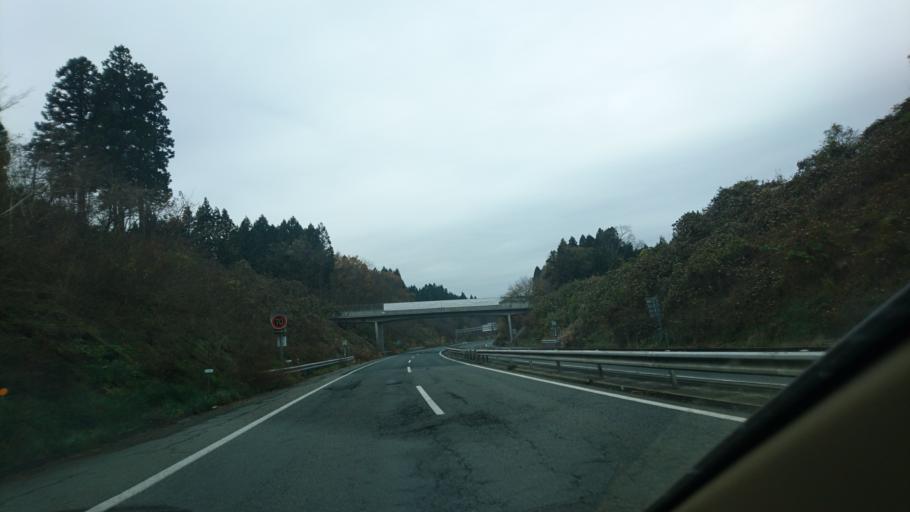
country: JP
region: Iwate
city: Kitakami
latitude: 39.2752
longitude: 141.0720
